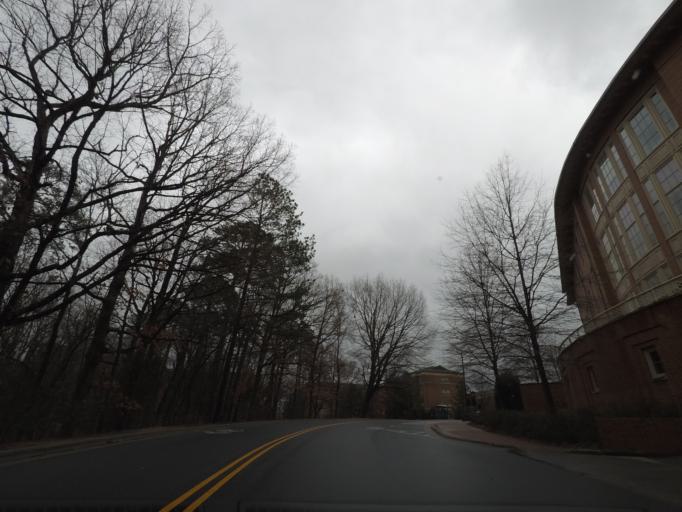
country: US
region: North Carolina
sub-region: Orange County
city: Chapel Hill
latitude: 35.9047
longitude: -79.0446
